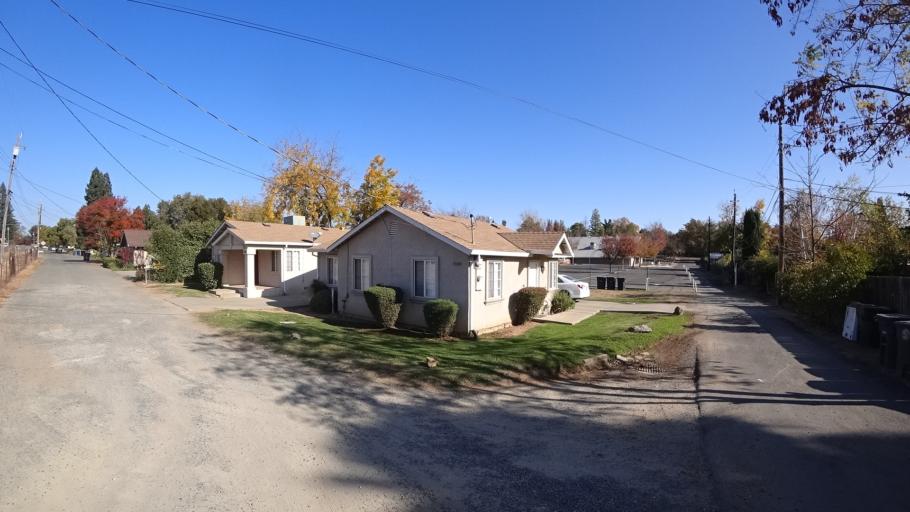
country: US
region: California
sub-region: Sacramento County
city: Citrus Heights
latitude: 38.6947
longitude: -121.2837
